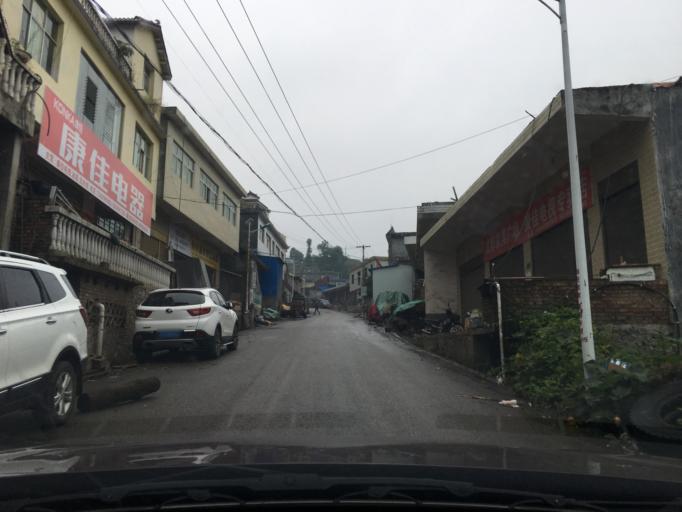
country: CN
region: Guizhou Sheng
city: Liupanshui
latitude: 26.0565
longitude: 105.1241
